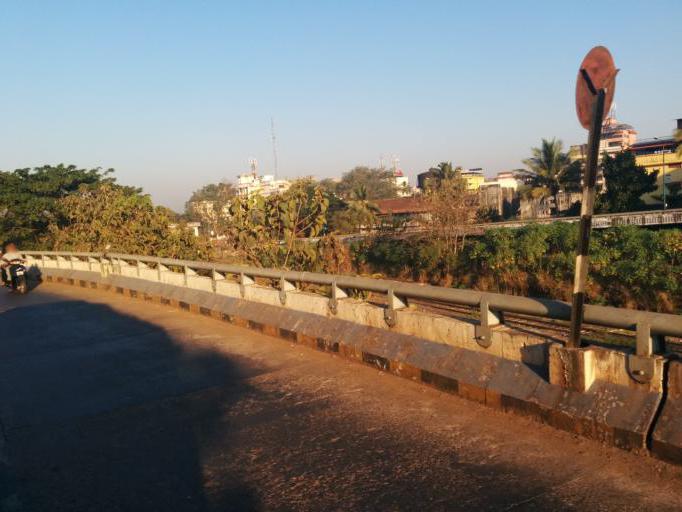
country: IN
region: Goa
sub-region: South Goa
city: Madgaon
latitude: 15.2687
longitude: 73.9603
